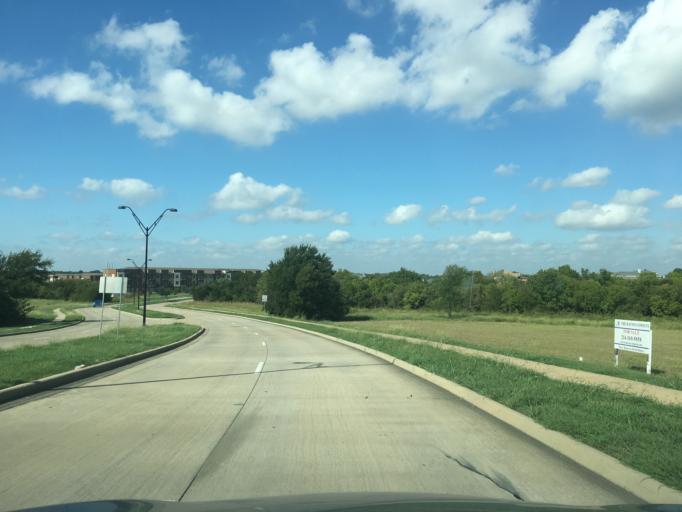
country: US
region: Texas
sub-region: Dallas County
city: Sachse
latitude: 32.9534
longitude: -96.5841
